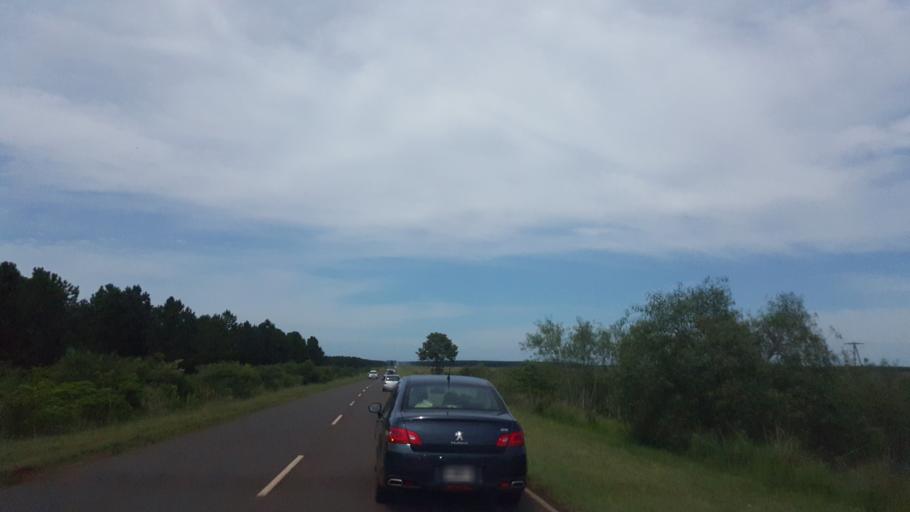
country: PY
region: Itapua
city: San Juan del Parana
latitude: -27.5080
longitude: -56.1300
